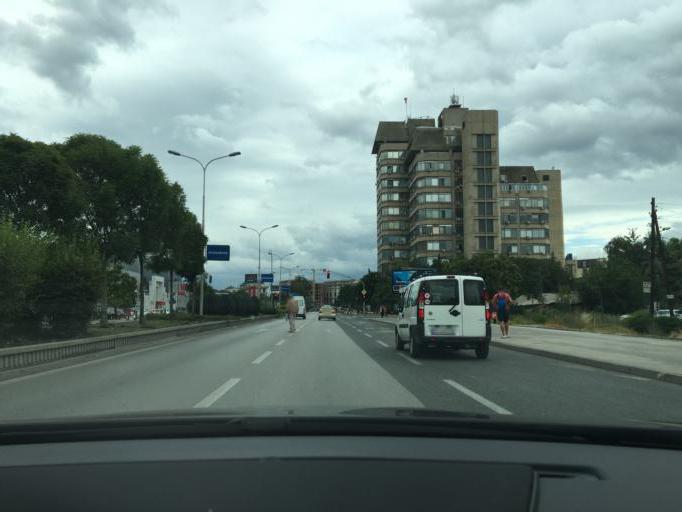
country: MK
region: Karpos
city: Skopje
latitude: 41.9926
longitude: 21.4441
